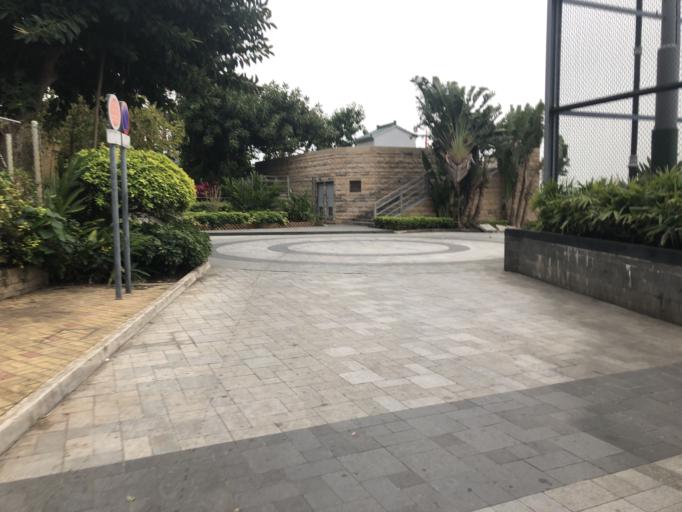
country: HK
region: Wanchai
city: Wan Chai
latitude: 22.2173
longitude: 114.2127
